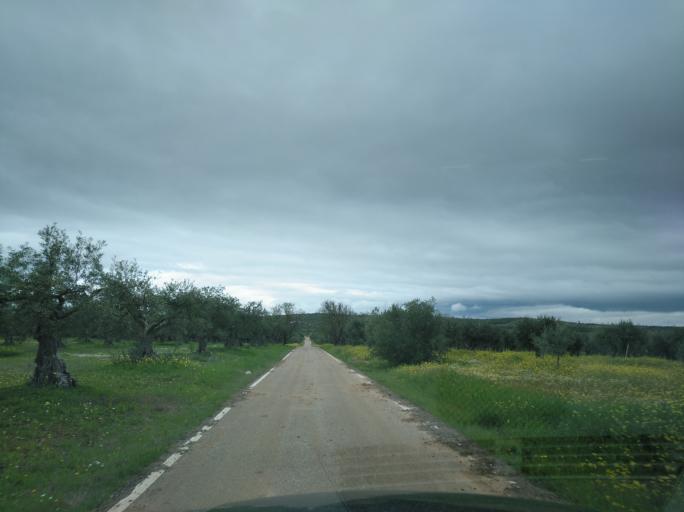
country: PT
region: Portalegre
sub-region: Campo Maior
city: Campo Maior
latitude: 38.9776
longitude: -7.0294
